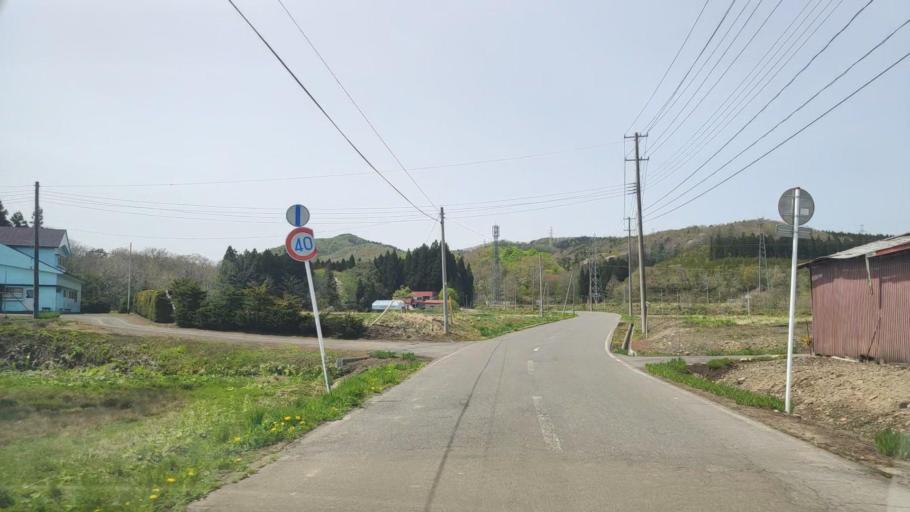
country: JP
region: Aomori
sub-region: Misawa Shi
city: Inuotose
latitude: 40.7889
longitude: 141.1034
